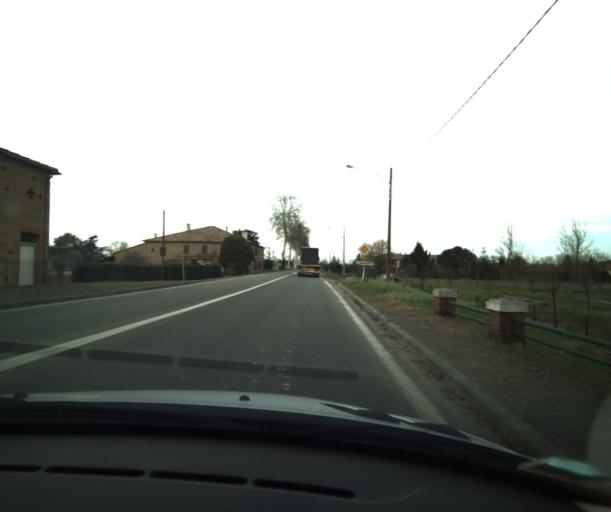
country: FR
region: Midi-Pyrenees
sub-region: Departement du Tarn-et-Garonne
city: Saint-Porquier
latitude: 44.0136
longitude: 1.1686
